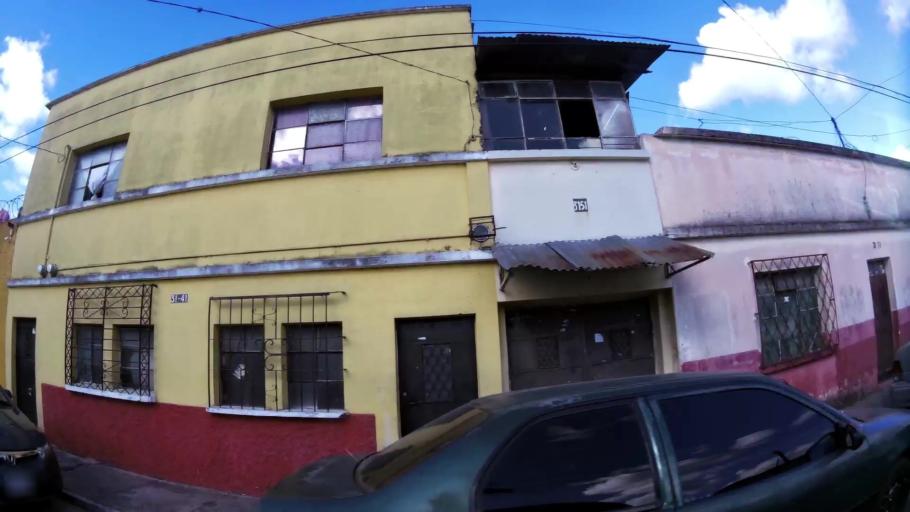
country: GT
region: Guatemala
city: Guatemala City
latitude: 14.6159
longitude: -90.5028
